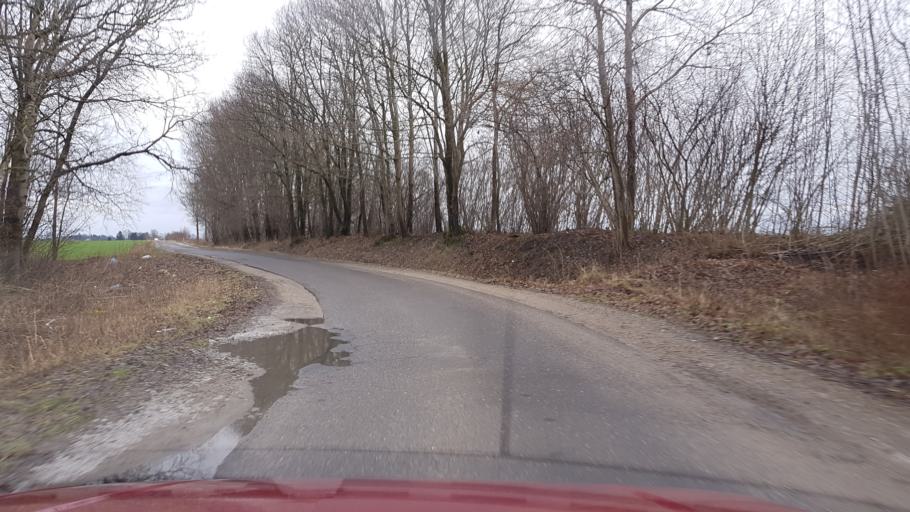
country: PL
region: West Pomeranian Voivodeship
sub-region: Powiat koszalinski
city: Mielno
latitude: 54.1482
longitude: 16.0300
